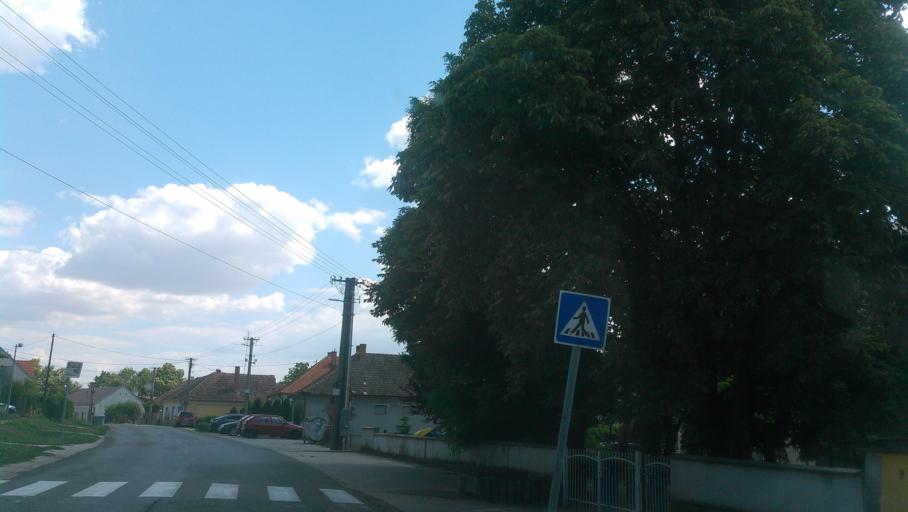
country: SK
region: Trnavsky
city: Leopoldov
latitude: 48.5082
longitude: 17.7244
